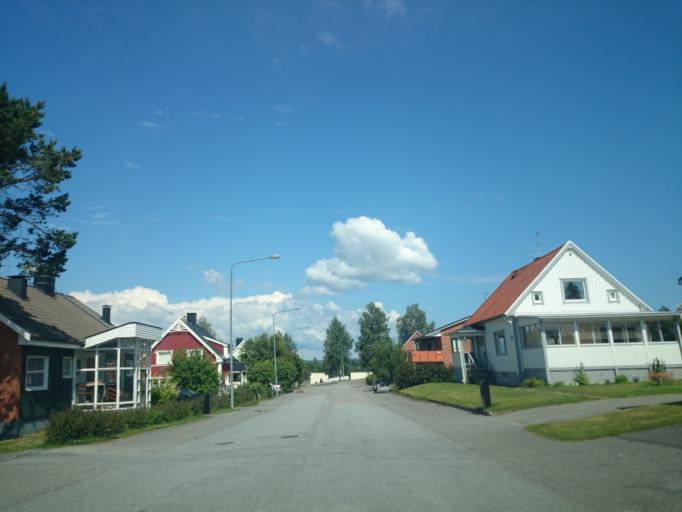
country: SE
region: Vaesternorrland
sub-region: Haernoesands Kommun
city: Haernoesand
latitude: 62.6399
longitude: 17.9570
